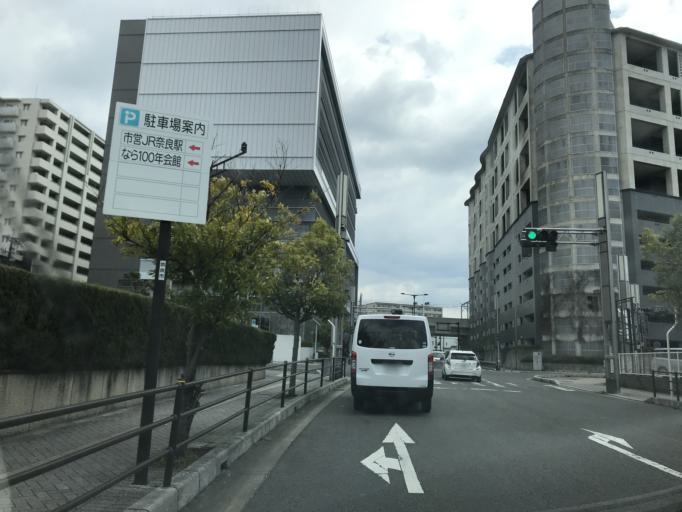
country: JP
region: Nara
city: Nara-shi
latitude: 34.6794
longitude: 135.8163
